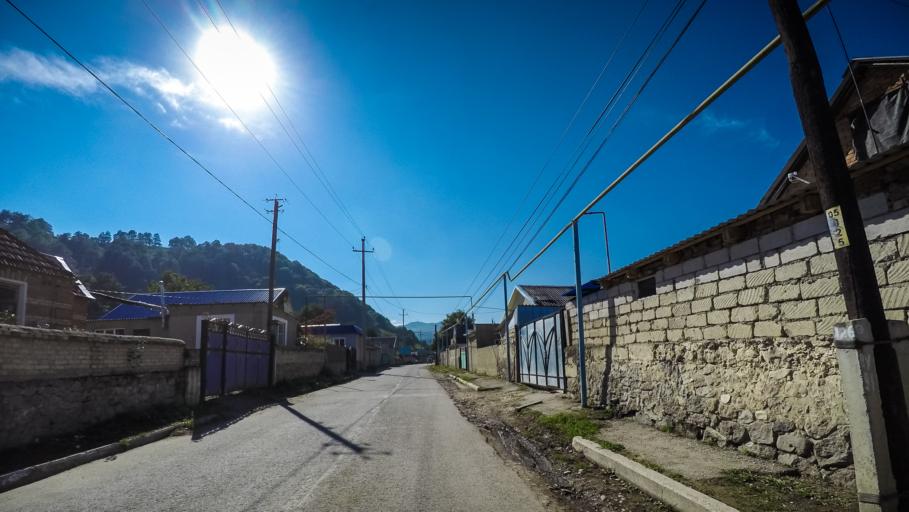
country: RU
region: Kabardino-Balkariya
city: Zhankhoteko
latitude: 43.4849
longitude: 43.2863
